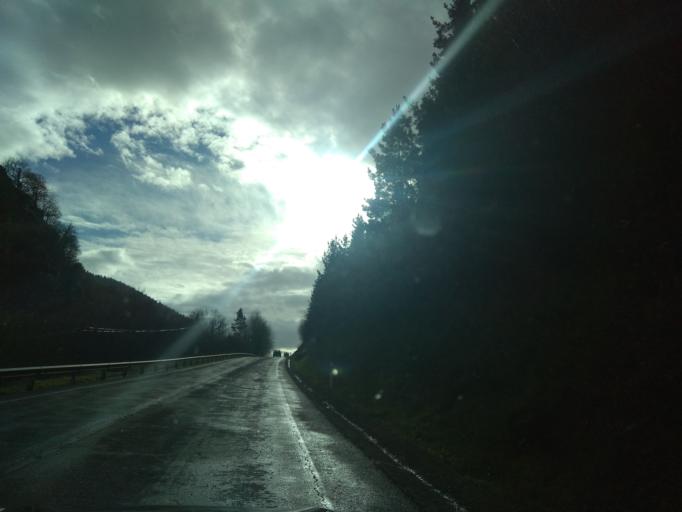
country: ES
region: Cantabria
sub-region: Provincia de Cantabria
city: San Pedro del Romeral
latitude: 43.1332
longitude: -3.9001
